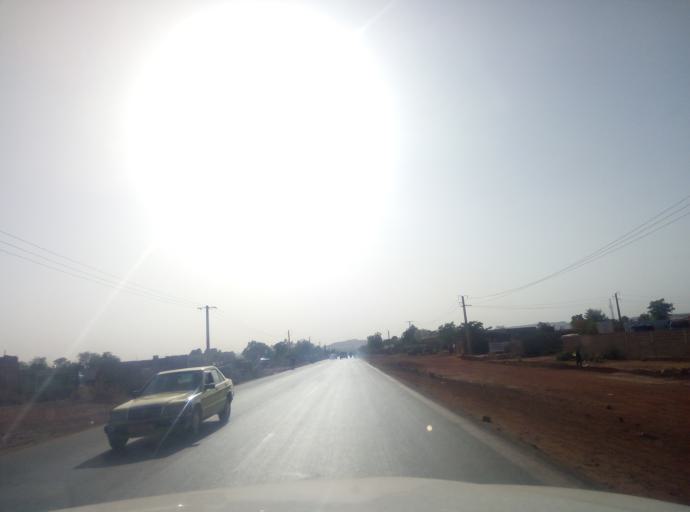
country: ML
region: Bamako
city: Bamako
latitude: 12.5842
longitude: -7.8233
